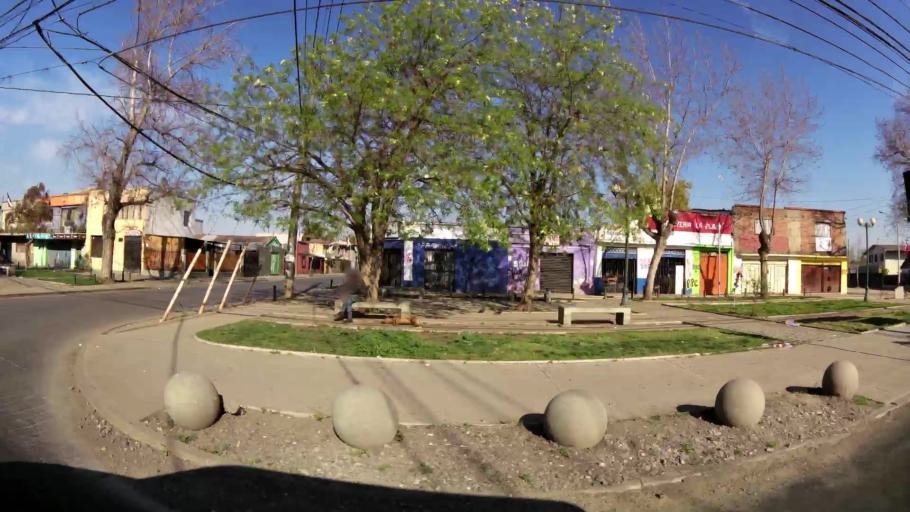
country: CL
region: Santiago Metropolitan
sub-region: Provincia de Santiago
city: Santiago
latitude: -33.3800
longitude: -70.6730
